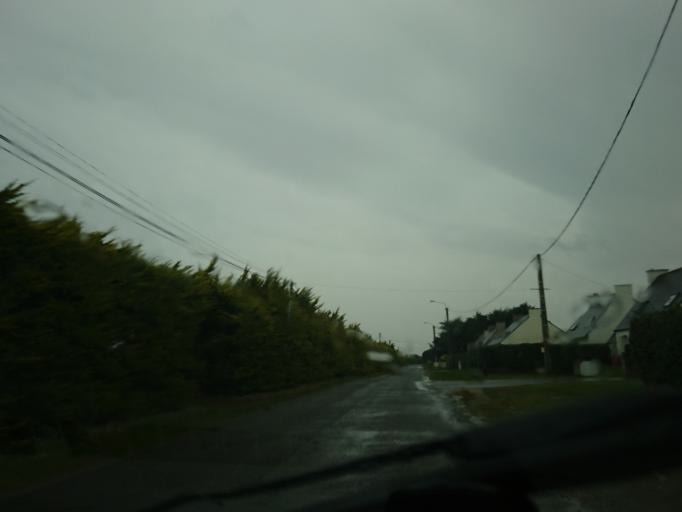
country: FR
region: Brittany
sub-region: Departement du Finistere
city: Guisseny
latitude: 48.6333
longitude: -4.4509
